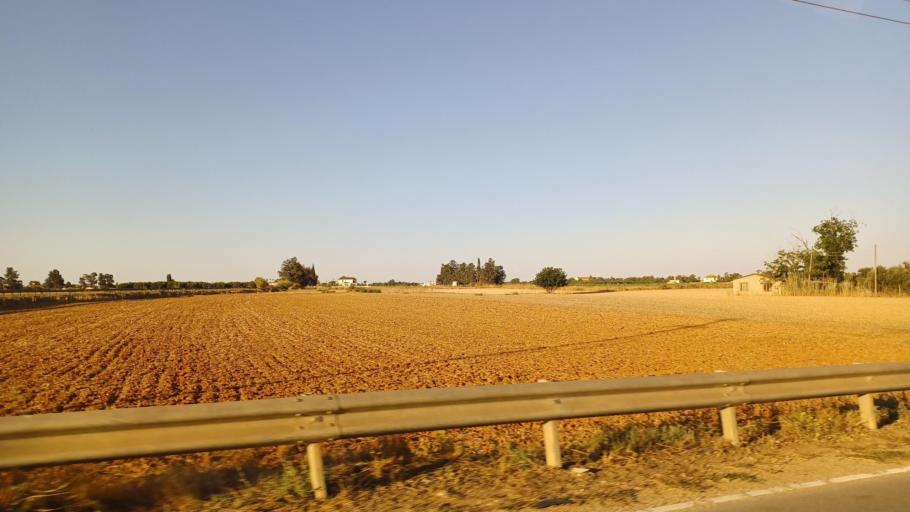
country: CY
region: Ammochostos
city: Achna
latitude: 35.0359
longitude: 33.7813
